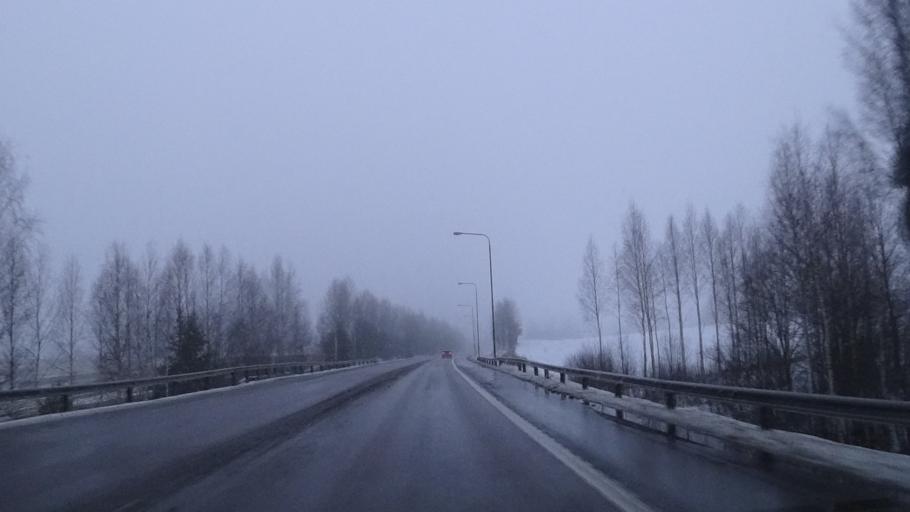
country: FI
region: Paijanne Tavastia
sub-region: Lahti
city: Hollola
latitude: 60.9818
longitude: 25.4655
